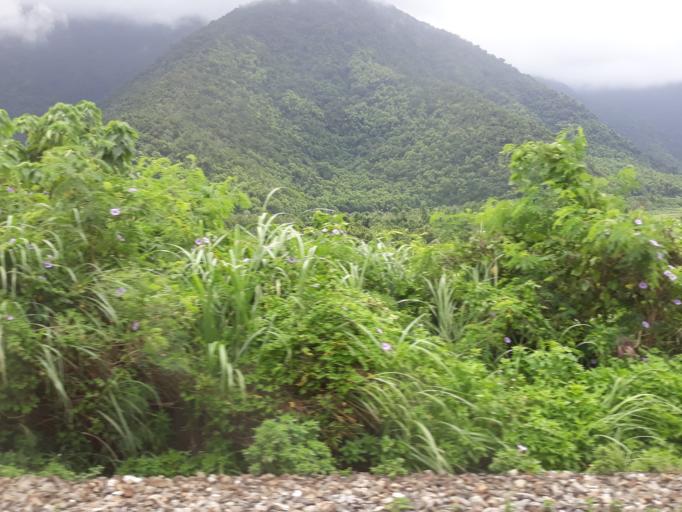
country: TW
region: Taiwan
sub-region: Yilan
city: Yilan
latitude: 24.4621
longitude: 121.8067
